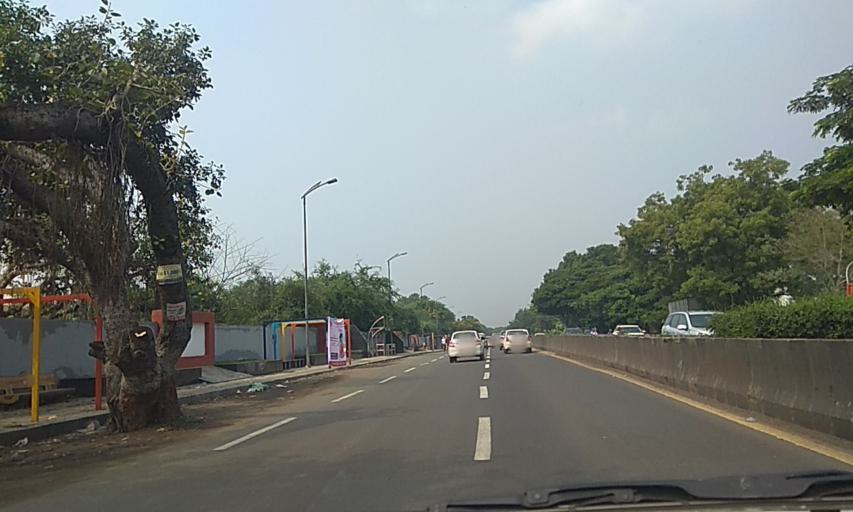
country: IN
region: Maharashtra
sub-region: Pune Division
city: Khadki
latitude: 18.5527
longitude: 73.8789
